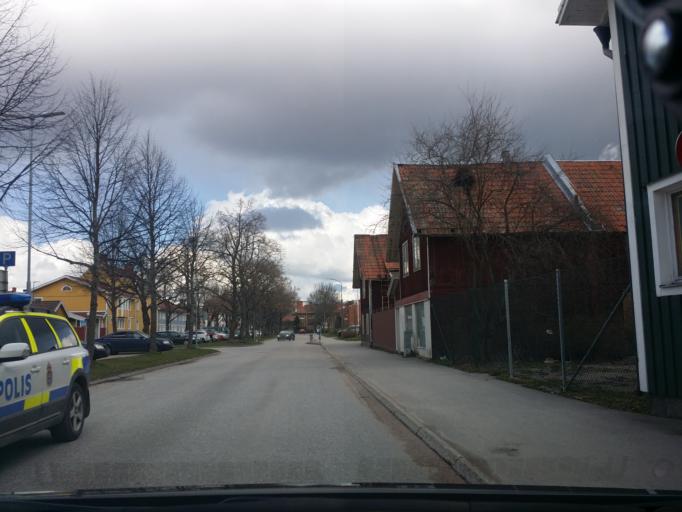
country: SE
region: Vaestmanland
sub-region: Sala Kommun
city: Sala
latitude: 59.9186
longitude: 16.6116
